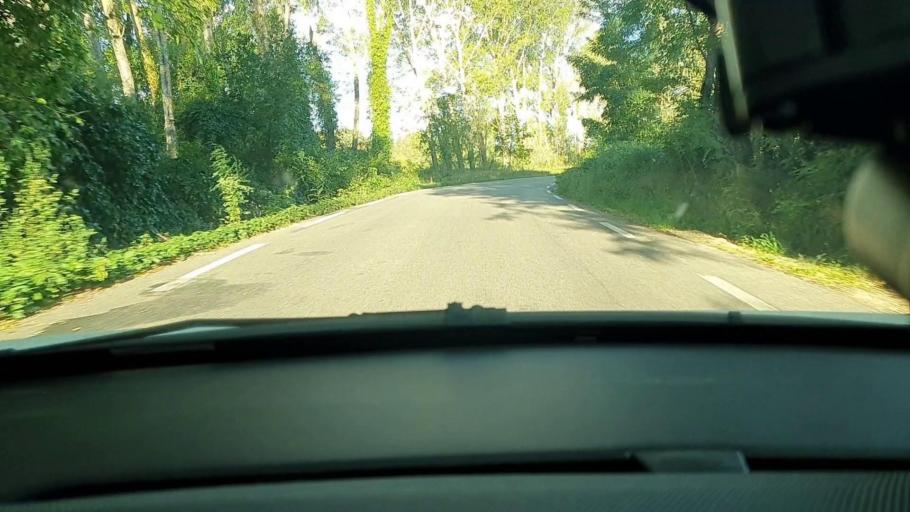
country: FR
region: Languedoc-Roussillon
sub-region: Departement du Gard
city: Saint-Ambroix
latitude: 44.2352
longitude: 4.2727
